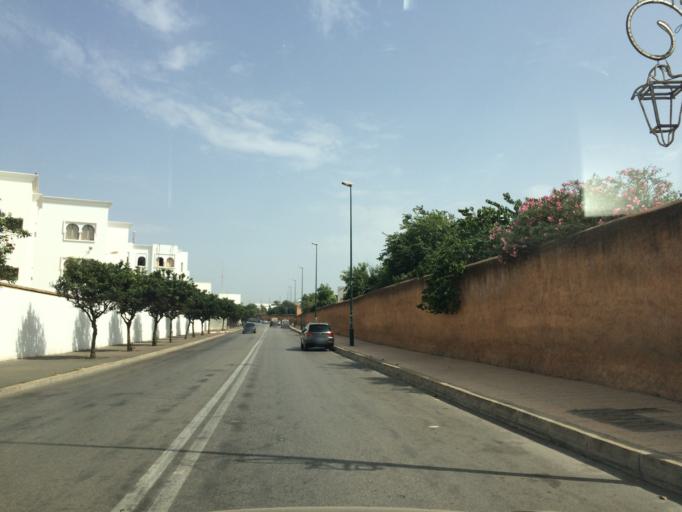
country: MA
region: Rabat-Sale-Zemmour-Zaer
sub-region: Rabat
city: Rabat
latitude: 34.0110
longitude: -6.8312
